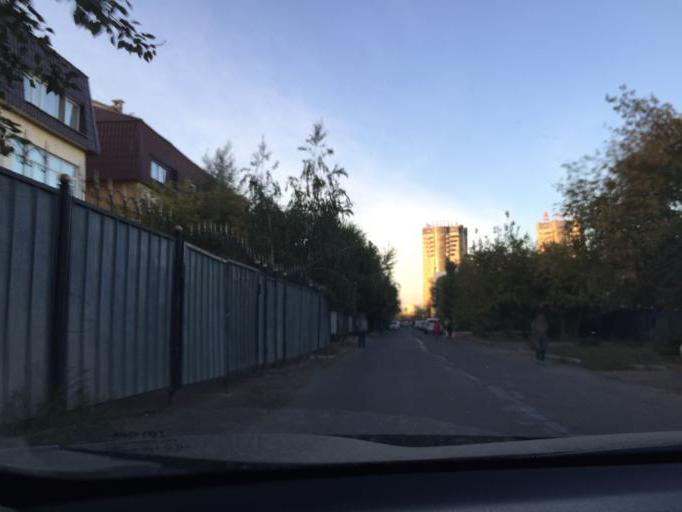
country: KZ
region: Astana Qalasy
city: Astana
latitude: 51.1425
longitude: 71.4205
